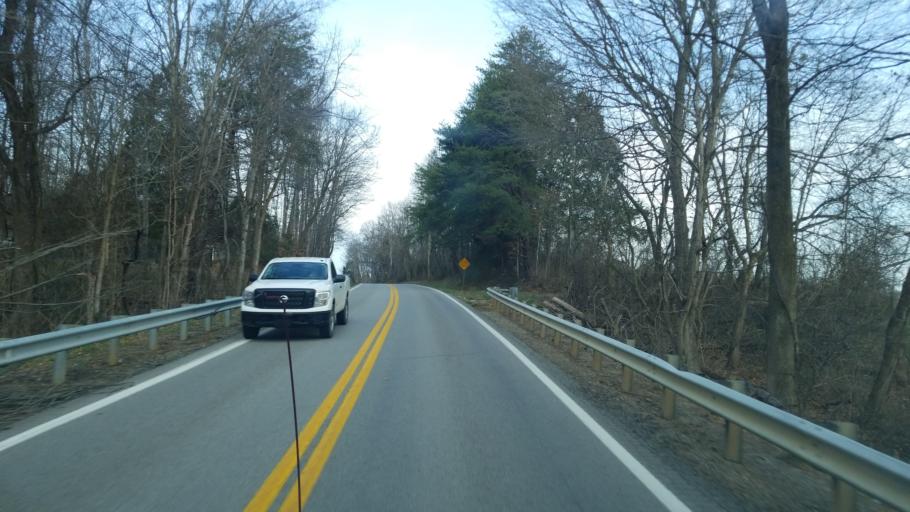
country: US
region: Kentucky
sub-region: Clinton County
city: Albany
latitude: 36.8183
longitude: -85.1834
